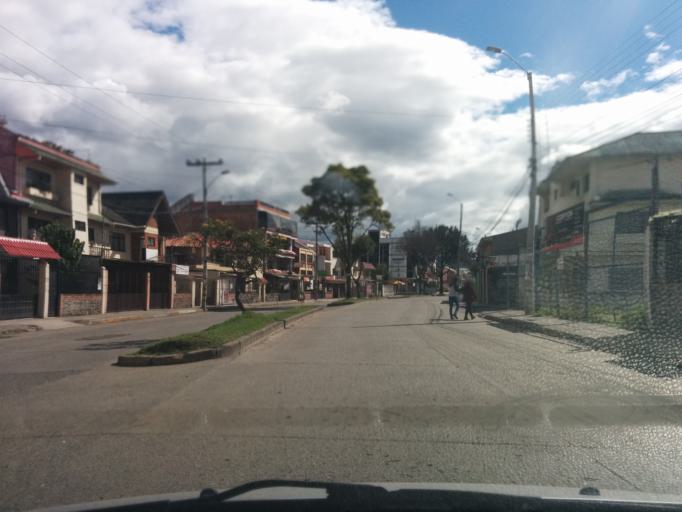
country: EC
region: Azuay
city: Cuenca
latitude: -2.9016
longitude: -78.9853
